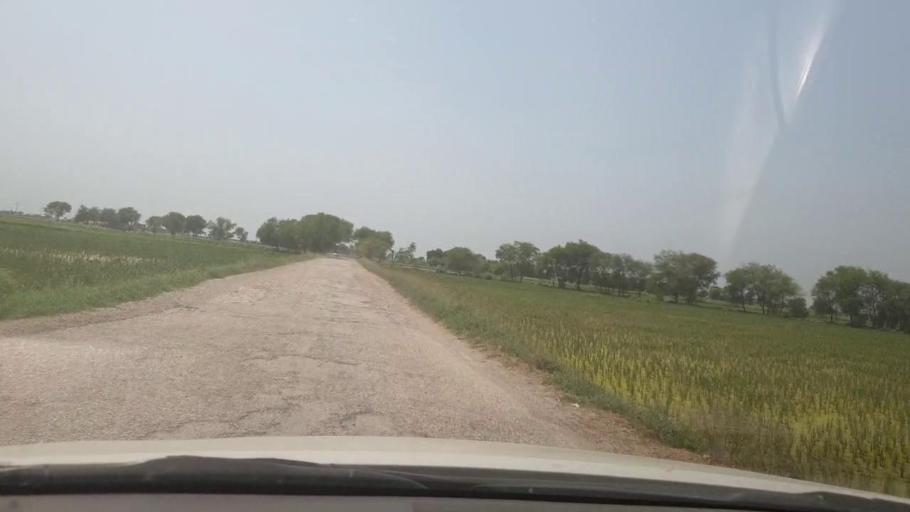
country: PK
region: Sindh
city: Shikarpur
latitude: 27.9939
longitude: 68.5808
